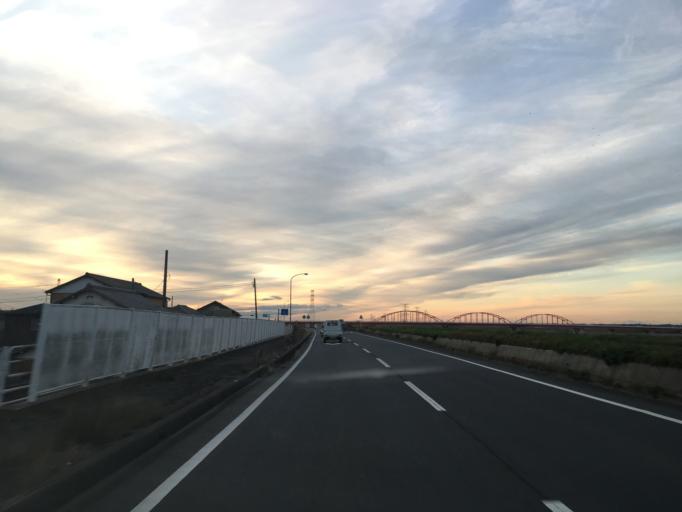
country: JP
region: Ibaraki
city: Inashiki
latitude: 35.9075
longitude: 140.4033
